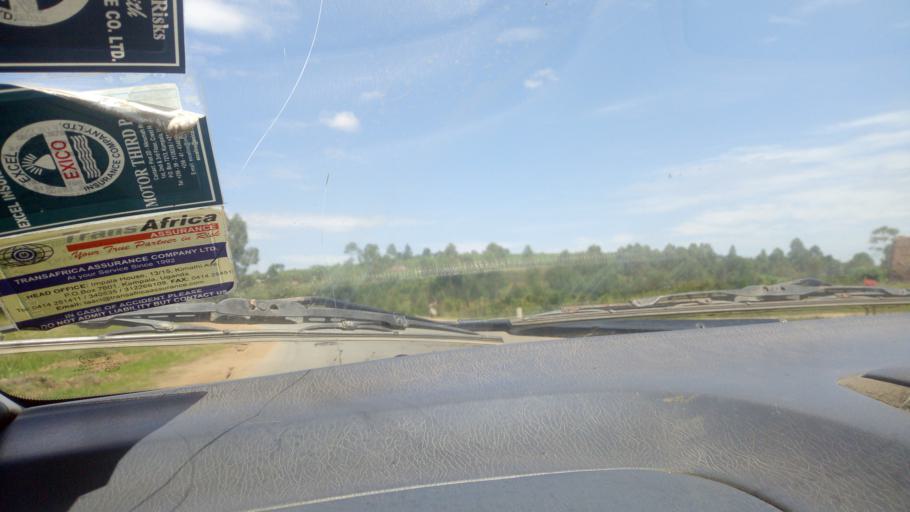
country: UG
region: Western Region
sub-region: Buhweju District
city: Buhweju
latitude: -0.2772
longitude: 30.5640
